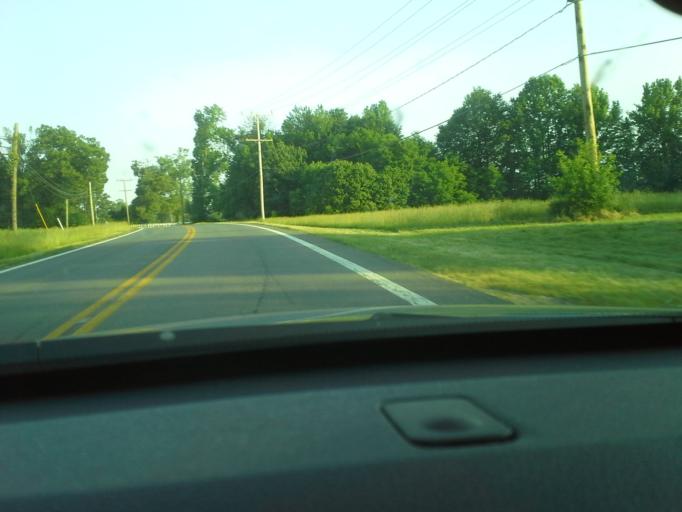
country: US
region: Maryland
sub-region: Anne Arundel County
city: Deale
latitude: 38.8262
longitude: -76.5614
